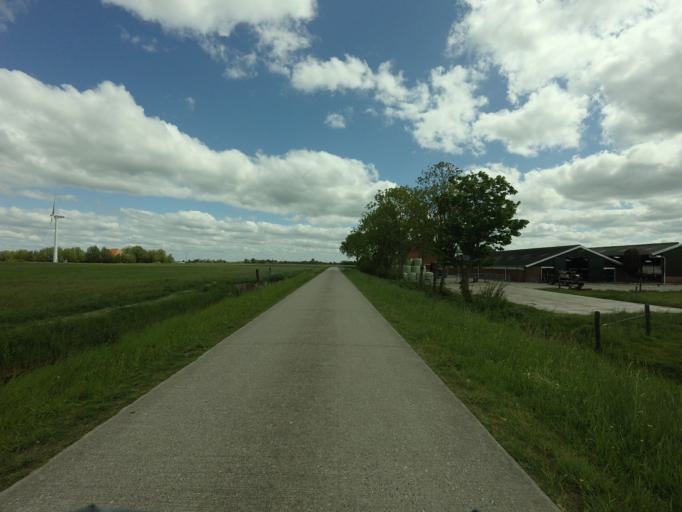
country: NL
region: Friesland
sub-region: Gemeente Franekeradeel
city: Tzum
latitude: 53.1264
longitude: 5.5523
